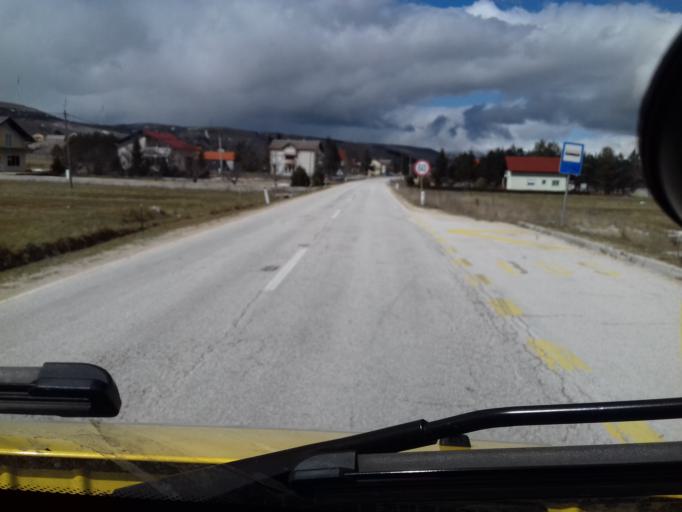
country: BA
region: Federation of Bosnia and Herzegovina
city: Dreznica
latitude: 43.6205
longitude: 17.2609
